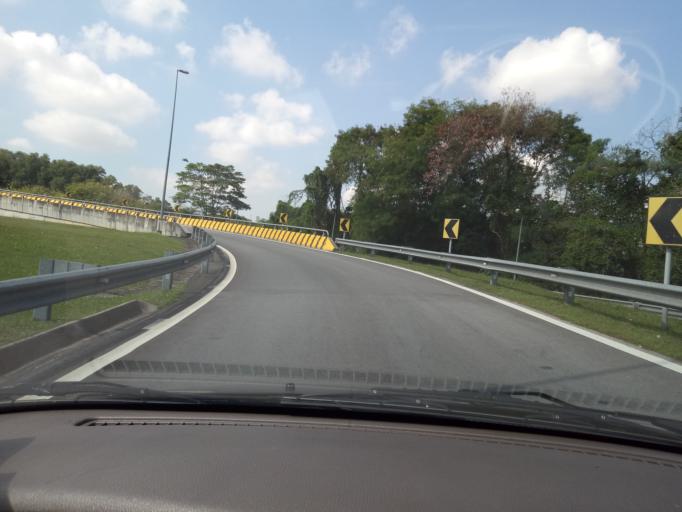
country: MY
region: Selangor
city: Kampong Baharu Balakong
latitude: 3.0622
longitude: 101.6828
